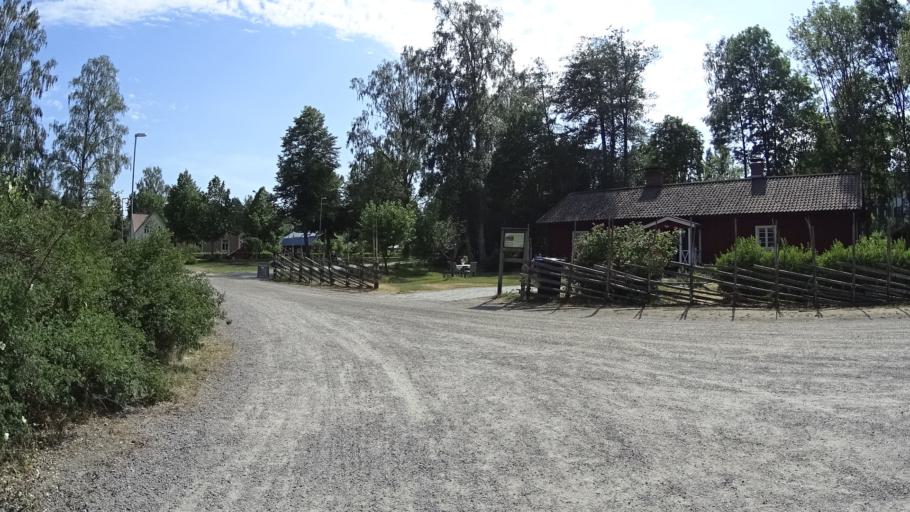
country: FI
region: Uusimaa
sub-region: Raaseporin
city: Karis
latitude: 60.0758
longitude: 23.6665
